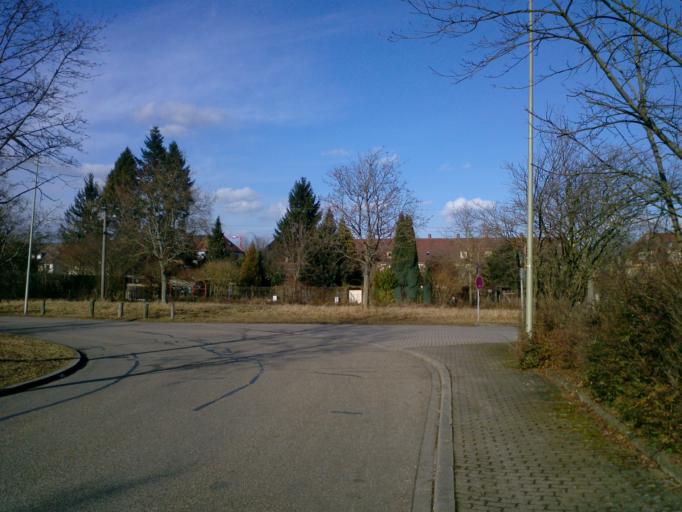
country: DE
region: Baden-Wuerttemberg
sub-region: Karlsruhe Region
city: Karlsruhe
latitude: 48.9918
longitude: 8.3752
